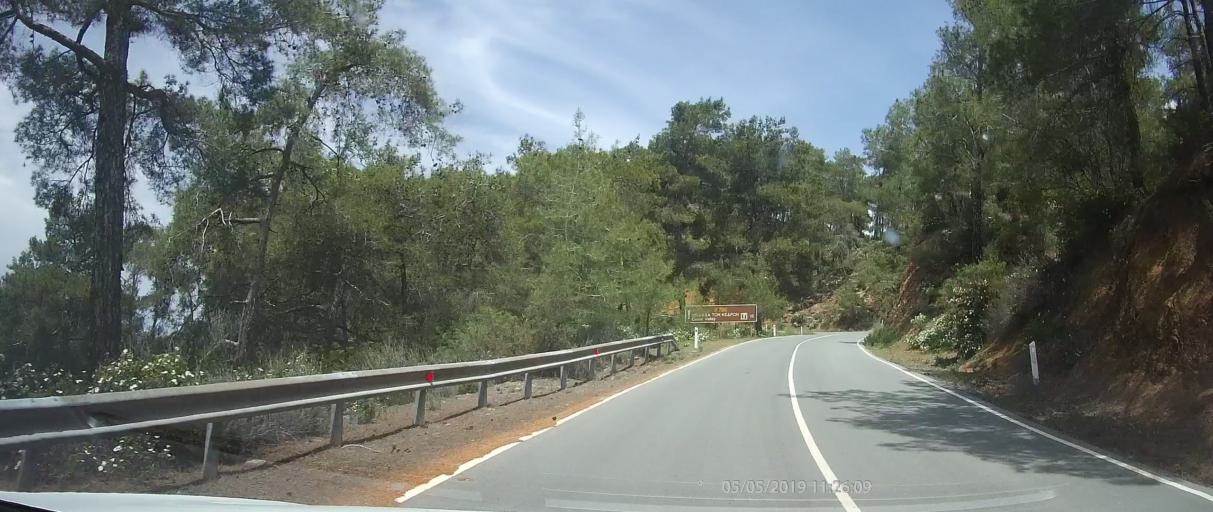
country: CY
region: Limassol
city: Pachna
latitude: 34.9269
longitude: 32.6473
